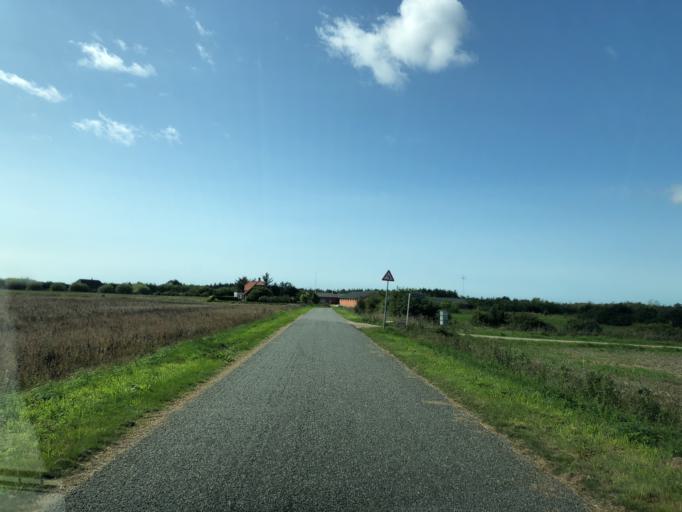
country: DK
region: Central Jutland
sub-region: Holstebro Kommune
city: Ulfborg
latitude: 56.2608
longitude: 8.1633
